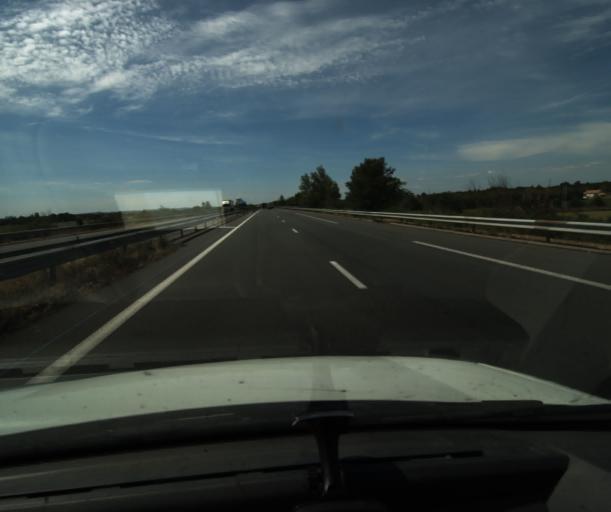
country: FR
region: Midi-Pyrenees
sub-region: Departement du Tarn-et-Garonne
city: Saint-Porquier
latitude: 44.0354
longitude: 1.1568
